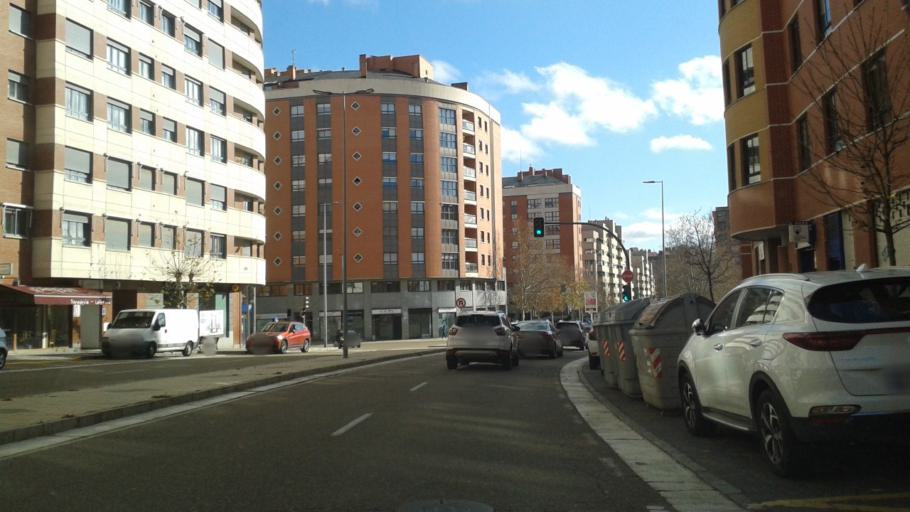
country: ES
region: Castille and Leon
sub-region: Provincia de Valladolid
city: Zaratan
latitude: 41.6361
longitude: -4.7621
